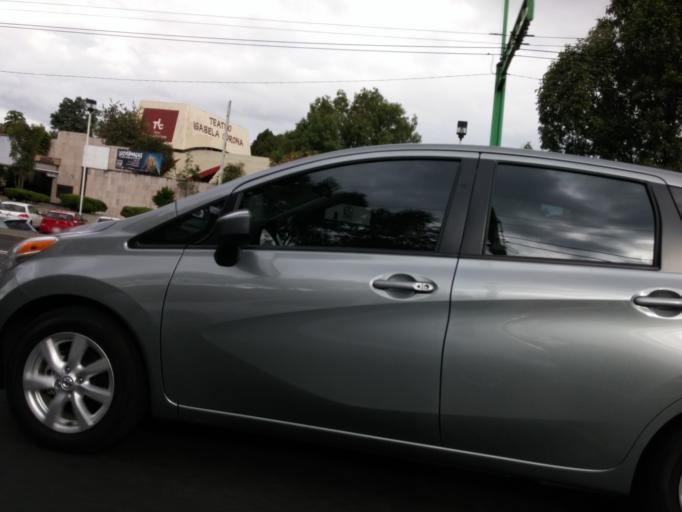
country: MX
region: Mexico City
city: Cuauhtemoc
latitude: 19.4525
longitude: -99.1384
